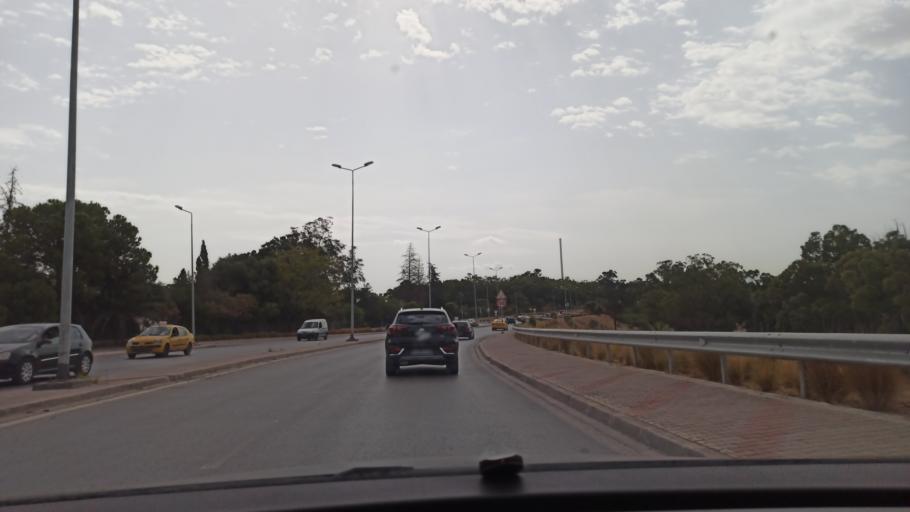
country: TN
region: Tunis
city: Tunis
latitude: 36.8297
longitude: 10.1648
